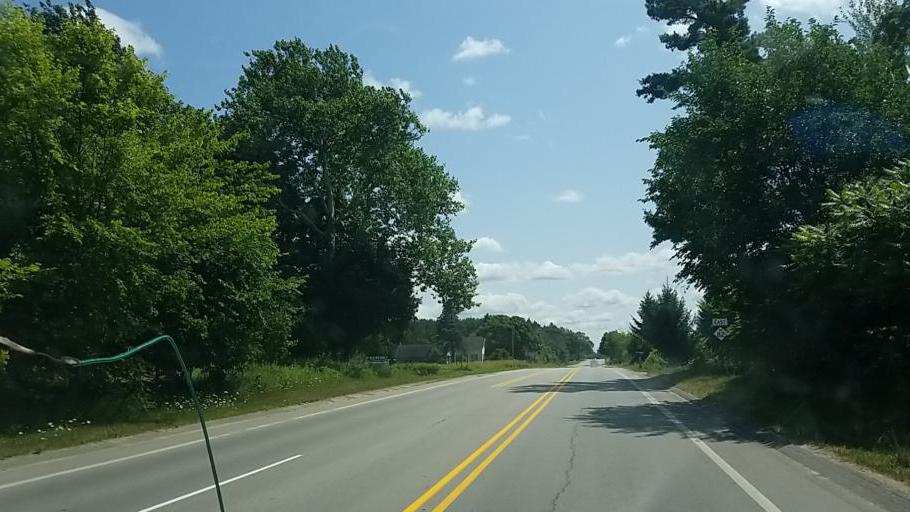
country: US
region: Michigan
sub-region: Newaygo County
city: Fremont
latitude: 43.4522
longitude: -85.9400
